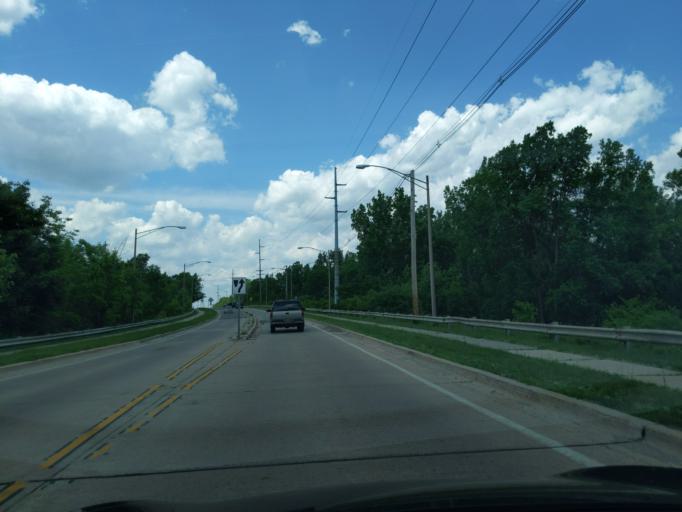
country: US
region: Michigan
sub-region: Ingham County
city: Lansing
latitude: 42.7169
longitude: -84.5225
